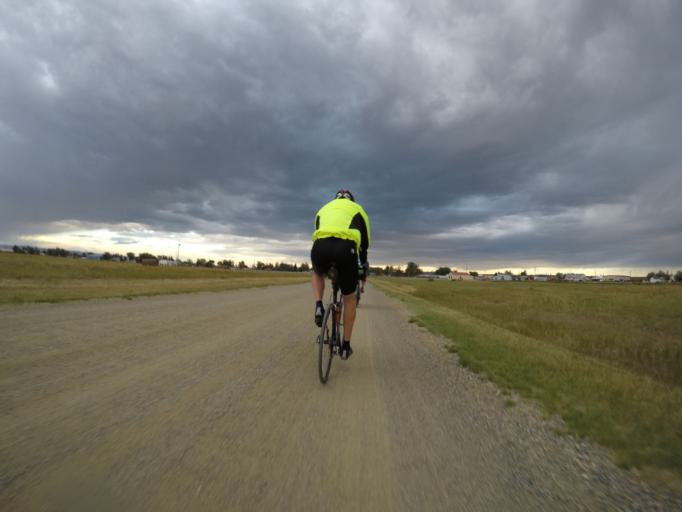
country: US
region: Wyoming
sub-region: Albany County
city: Laramie
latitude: 41.7425
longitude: -105.9724
